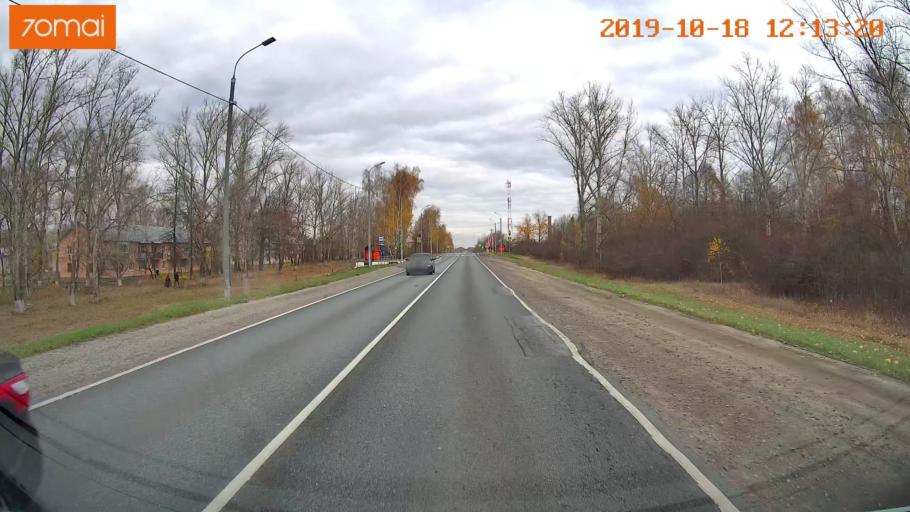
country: RU
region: Rjazan
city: Zakharovo
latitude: 54.4201
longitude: 39.3689
